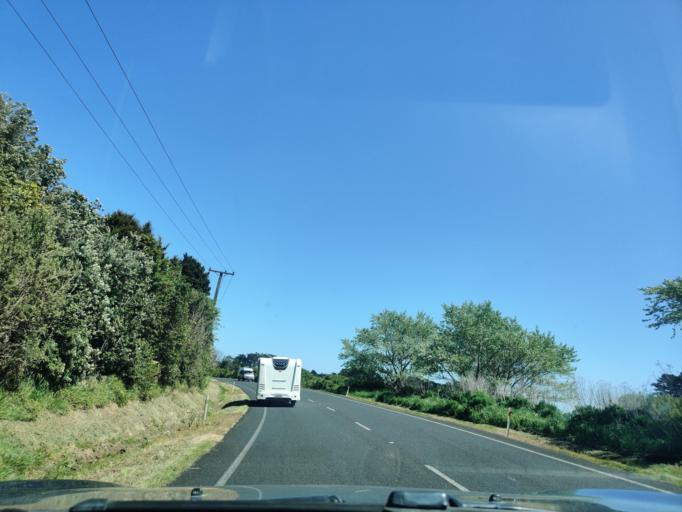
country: NZ
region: Taranaki
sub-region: South Taranaki District
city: Patea
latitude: -39.8074
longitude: 174.7592
